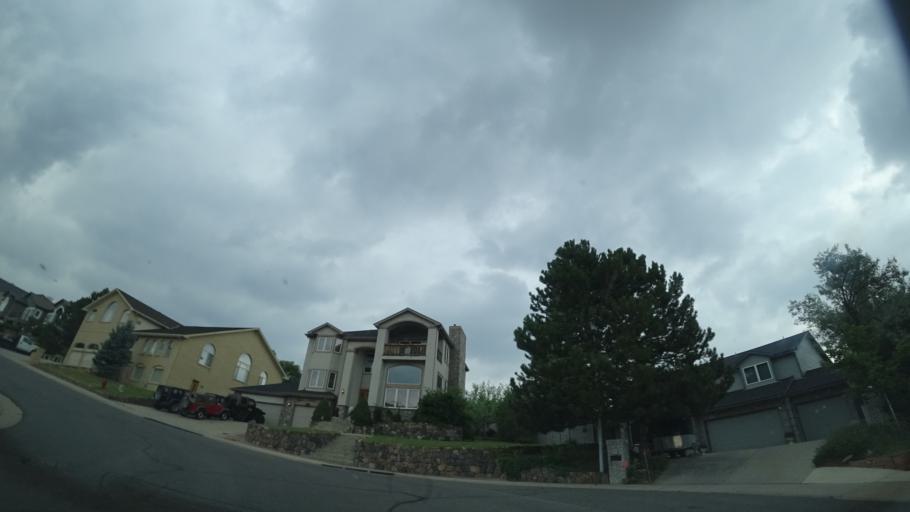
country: US
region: Colorado
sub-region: Jefferson County
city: West Pleasant View
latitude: 39.7005
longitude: -105.1538
